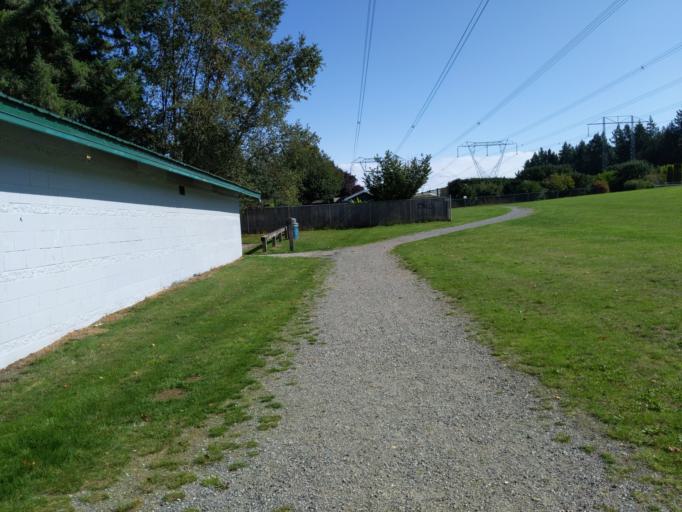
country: CA
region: British Columbia
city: Langley
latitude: 49.0893
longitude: -122.6780
